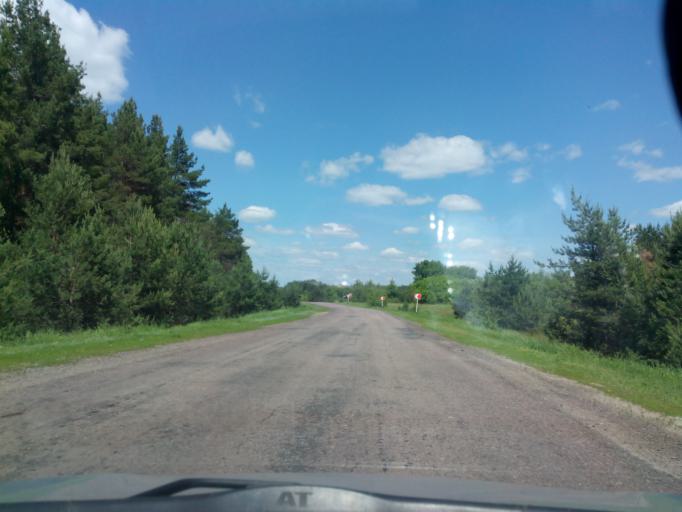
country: RU
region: Voronezj
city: Ternovka
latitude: 51.7192
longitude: 41.5185
